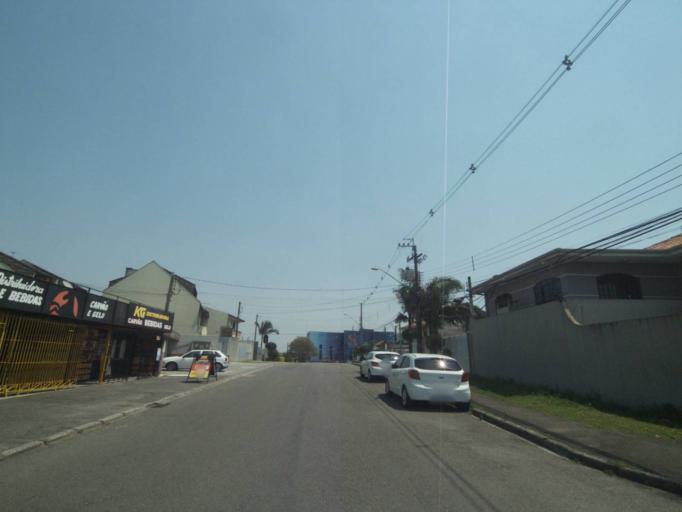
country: BR
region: Parana
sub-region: Sao Jose Dos Pinhais
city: Sao Jose dos Pinhais
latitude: -25.5078
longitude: -49.2723
